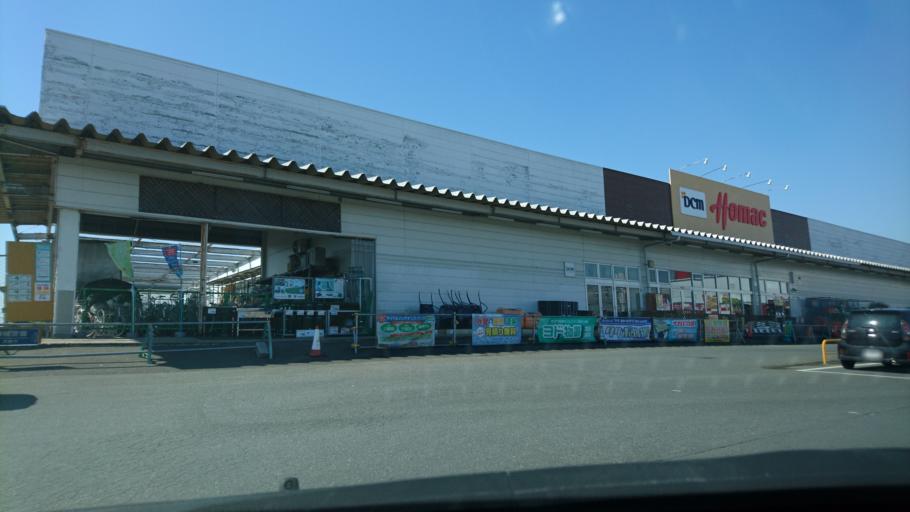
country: JP
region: Iwate
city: Ichinoseki
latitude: 38.7692
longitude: 141.1557
